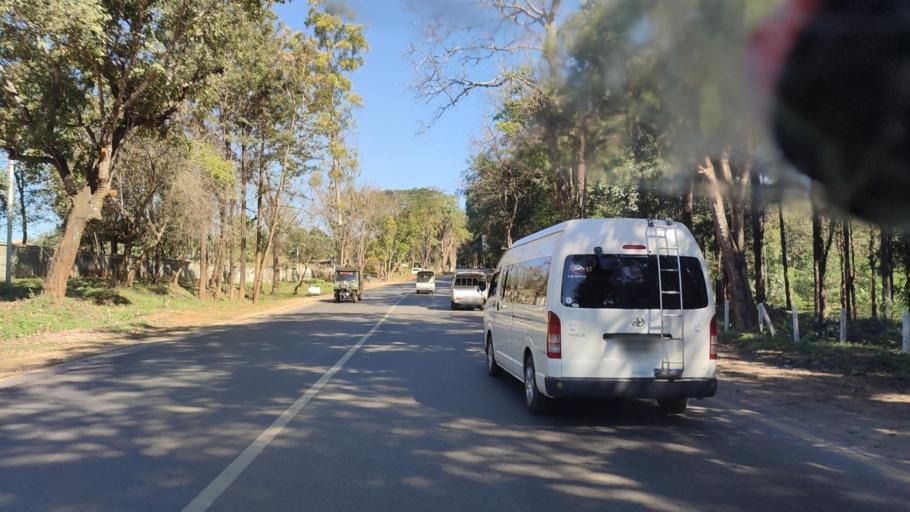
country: MM
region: Mandalay
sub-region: Pyin Oo Lwin District
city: Pyin Oo Lwin
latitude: 22.0024
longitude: 96.4328
